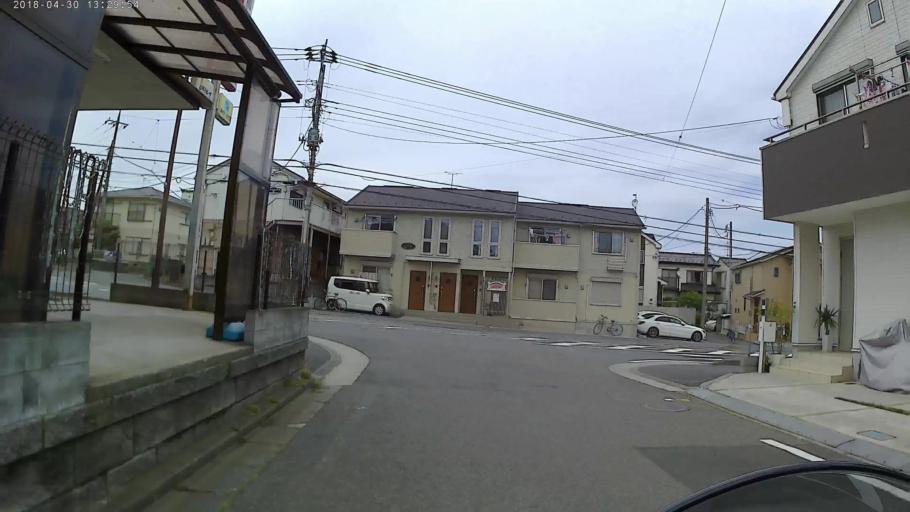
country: JP
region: Tokyo
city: Hachioji
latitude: 35.5911
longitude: 139.3227
